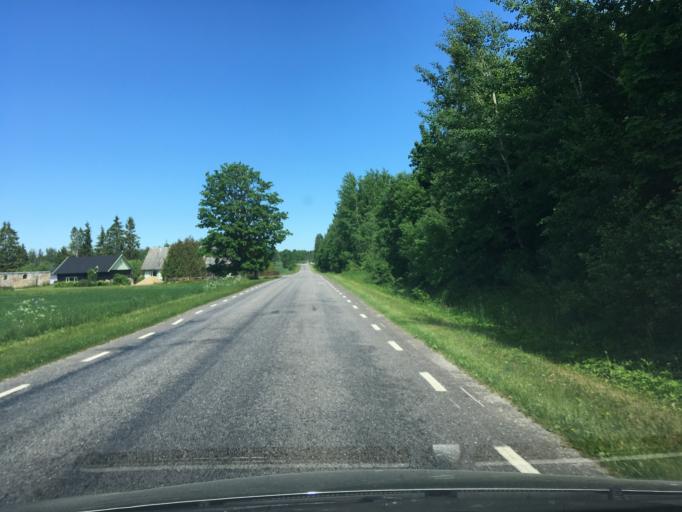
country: EE
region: Raplamaa
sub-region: Rapla vald
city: Rapla
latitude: 59.0627
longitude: 24.9119
